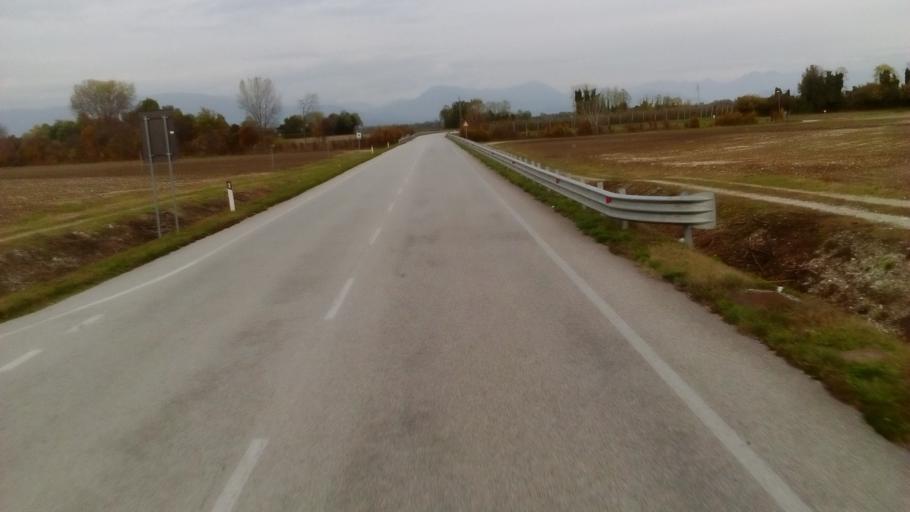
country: IT
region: Friuli Venezia Giulia
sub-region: Provincia di Pordenone
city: Vivaro
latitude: 46.0894
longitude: 12.7794
